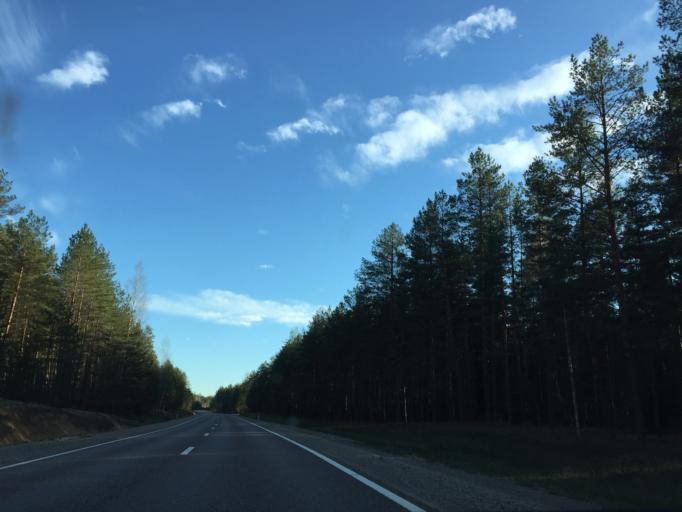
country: LV
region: Strenci
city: Seda
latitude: 57.6671
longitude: 25.8757
